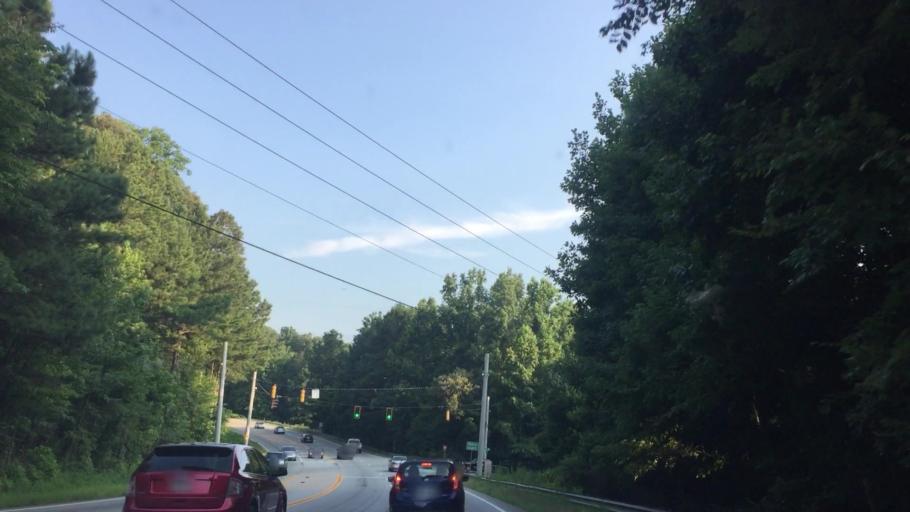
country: US
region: Georgia
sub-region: DeKalb County
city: Pine Mountain
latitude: 33.6471
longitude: -84.1876
